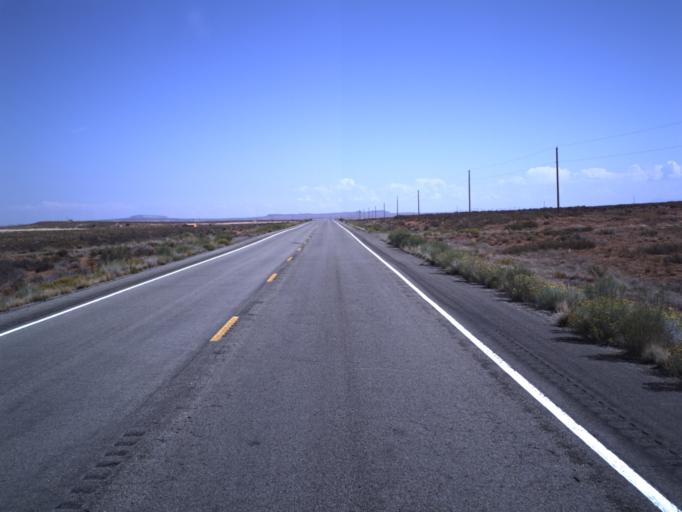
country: US
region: Utah
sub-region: San Juan County
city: Blanding
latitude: 37.0290
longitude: -109.5976
